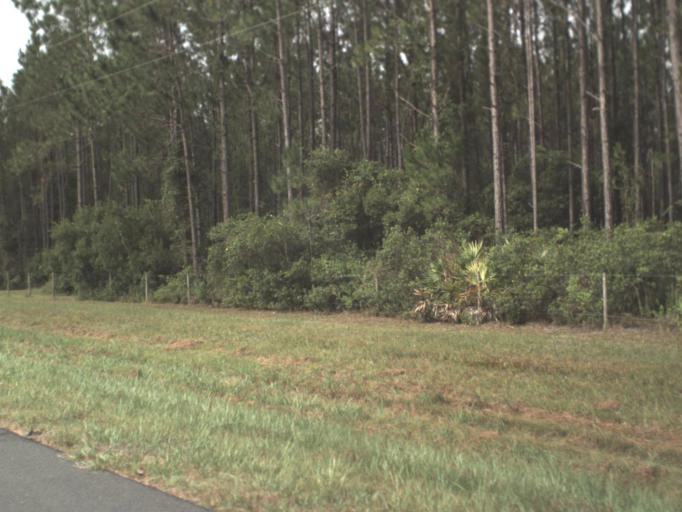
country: US
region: Florida
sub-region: Hamilton County
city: Jasper
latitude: 30.5047
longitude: -82.6670
